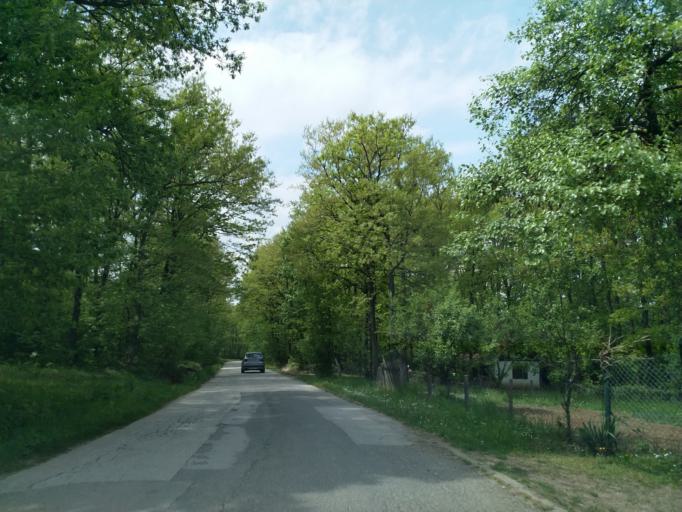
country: RS
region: Central Serbia
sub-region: Pomoravski Okrug
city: Paracin
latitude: 43.9493
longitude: 21.4894
